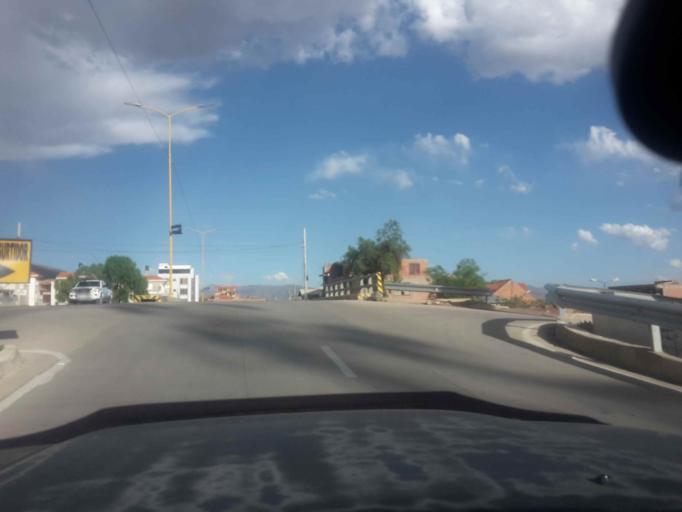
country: BO
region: Cochabamba
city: Cochabamba
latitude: -17.3449
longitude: -66.1994
